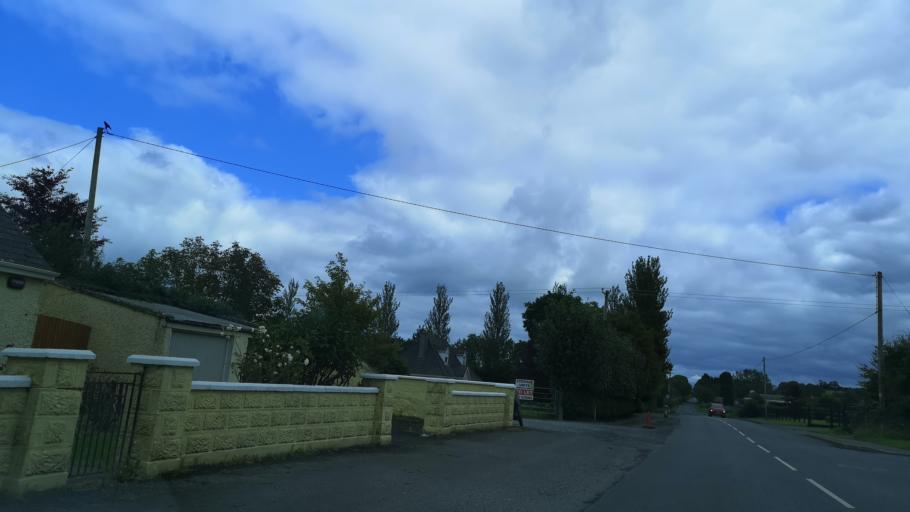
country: IE
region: Leinster
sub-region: Uibh Fhaili
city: Ferbane
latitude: 53.2247
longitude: -7.8739
